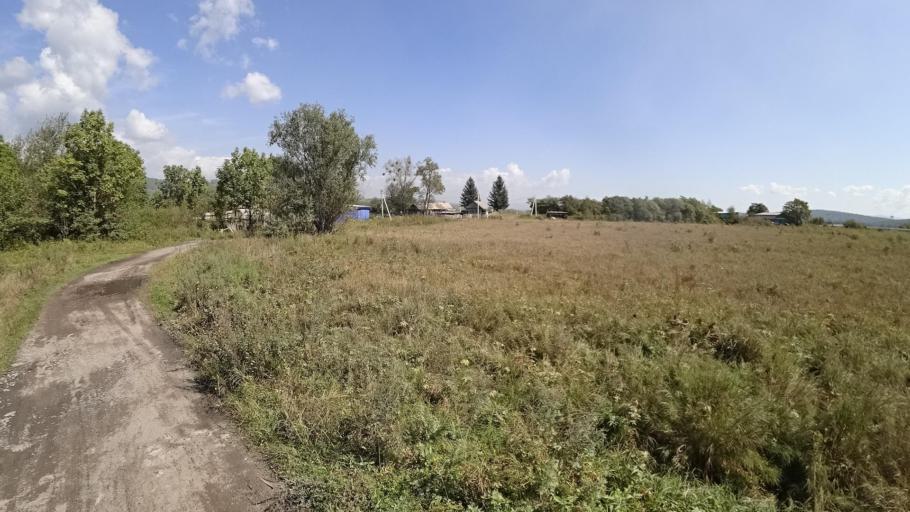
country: RU
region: Jewish Autonomous Oblast
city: Londoko
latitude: 49.0041
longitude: 131.9405
